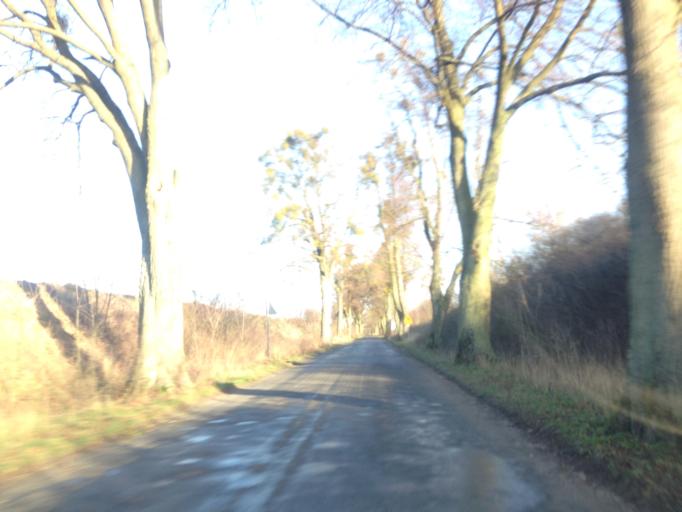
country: PL
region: Kujawsko-Pomorskie
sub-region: Powiat grudziadzki
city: Swiecie nad Osa
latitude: 53.4491
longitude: 19.1415
